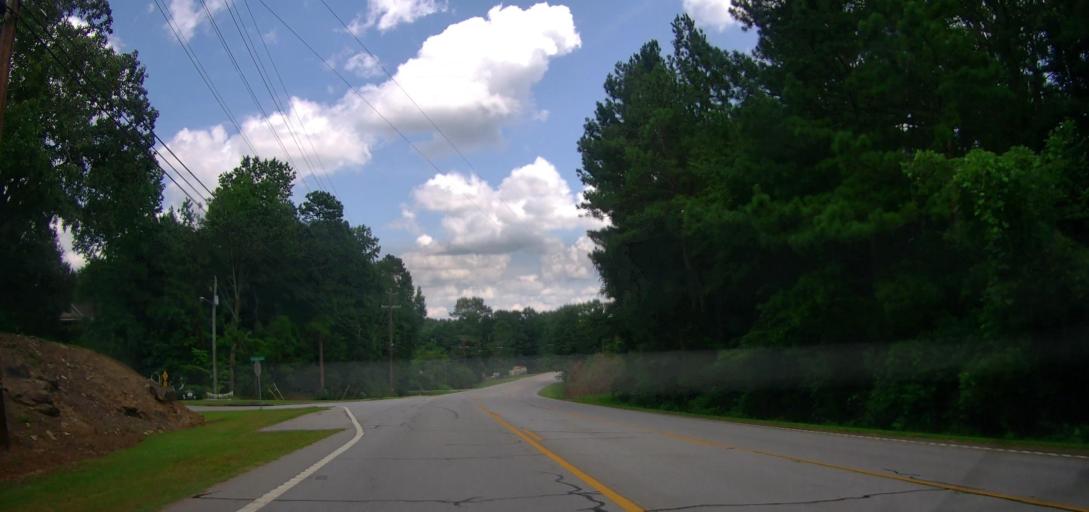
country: US
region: Georgia
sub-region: Heard County
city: Franklin
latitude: 33.2697
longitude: -85.0854
